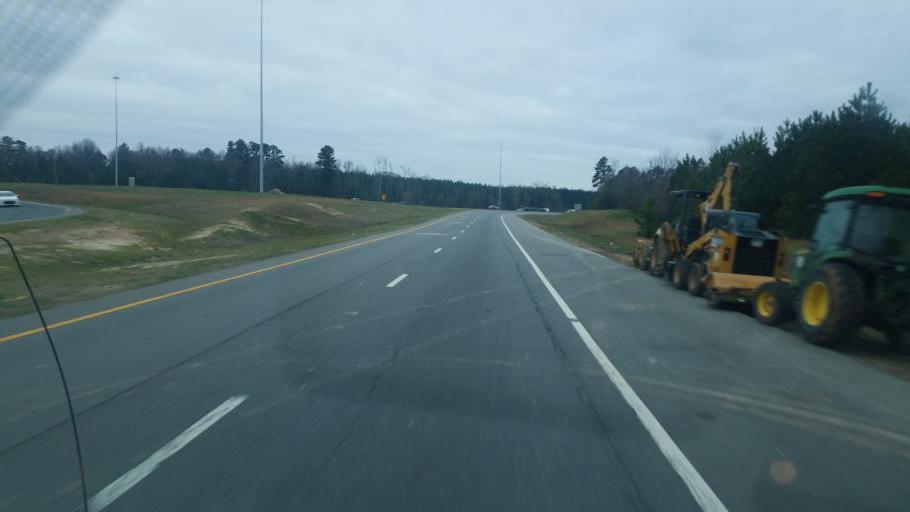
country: US
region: North Carolina
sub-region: Mecklenburg County
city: Huntersville
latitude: 35.3655
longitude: -80.8449
